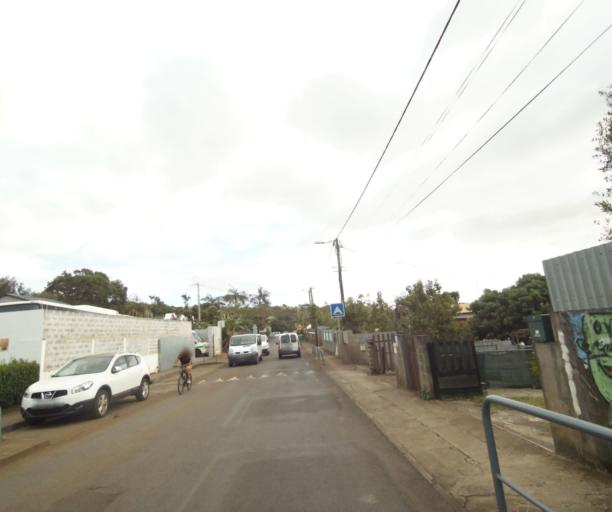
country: RE
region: Reunion
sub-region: Reunion
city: Saint-Paul
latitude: -21.0474
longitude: 55.2845
